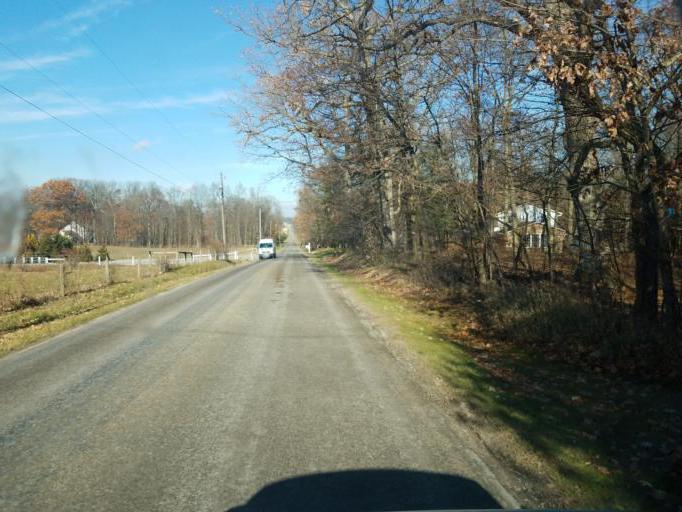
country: US
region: Ohio
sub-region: Wayne County
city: Apple Creek
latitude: 40.7512
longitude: -81.7752
